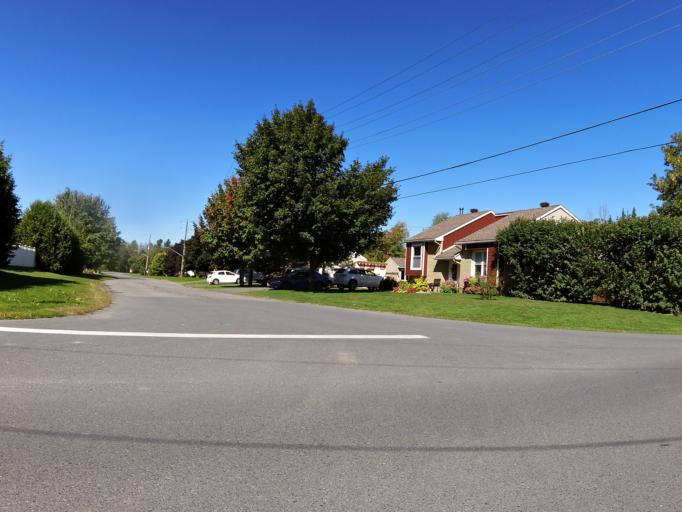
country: CA
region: Ontario
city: Casselman
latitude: 45.2668
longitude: -75.2787
